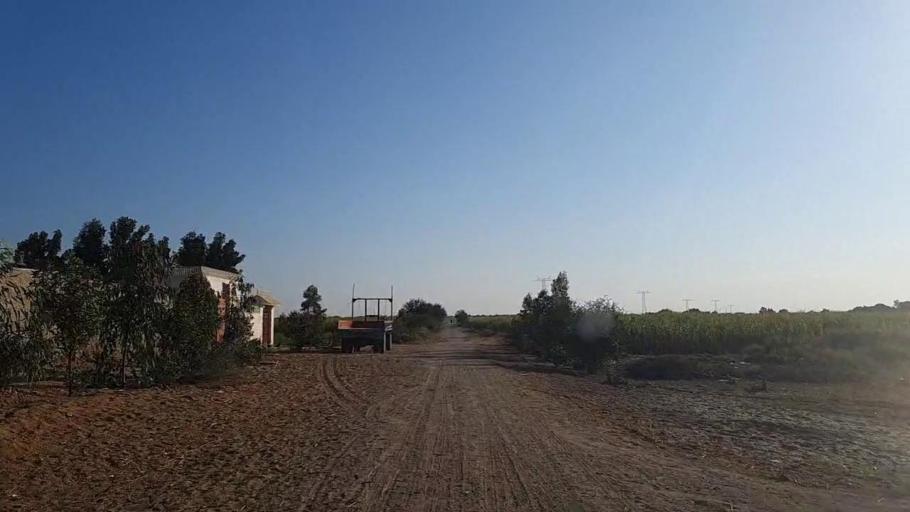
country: PK
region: Sindh
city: Khadro
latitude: 26.2702
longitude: 68.8603
